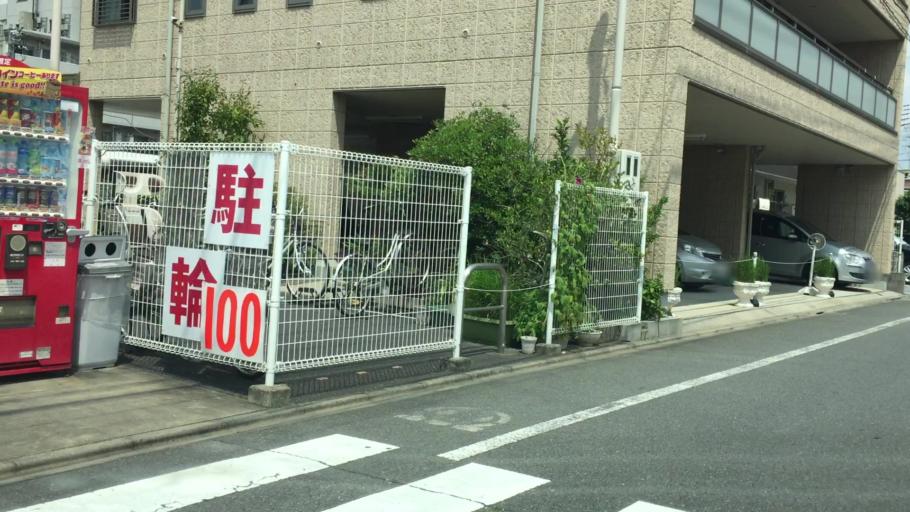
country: JP
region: Saitama
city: Soka
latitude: 35.7853
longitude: 139.8230
